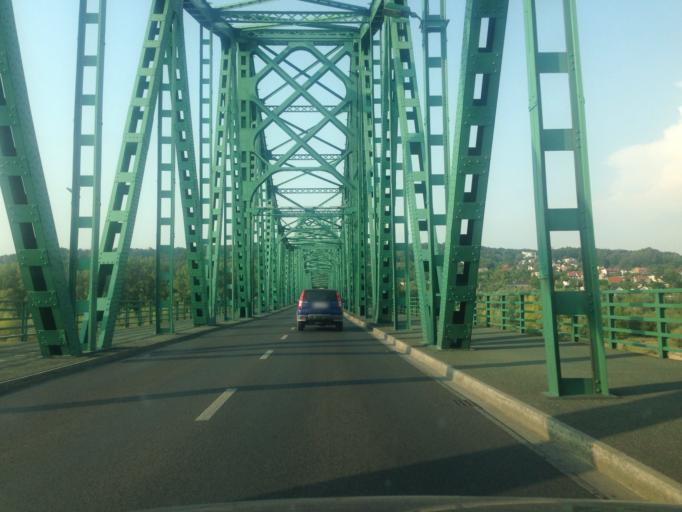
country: PL
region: Kujawsko-Pomorskie
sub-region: Wloclawek
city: Wloclawek
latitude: 52.6651
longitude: 19.0717
